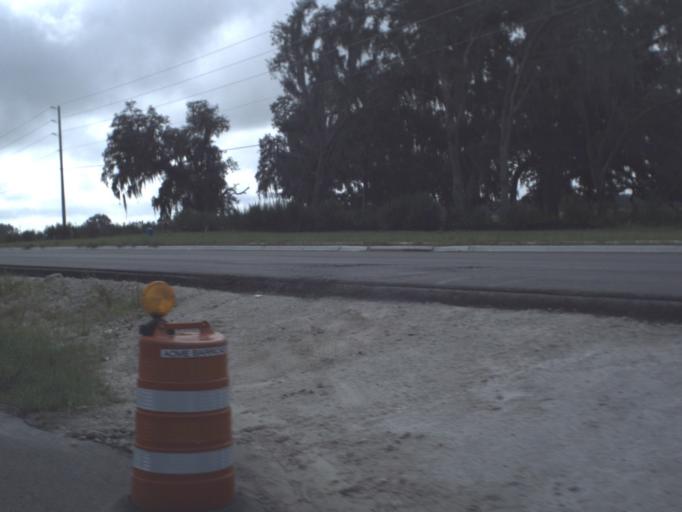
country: US
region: Florida
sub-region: Pasco County
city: San Antonio
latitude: 28.3257
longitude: -82.3190
